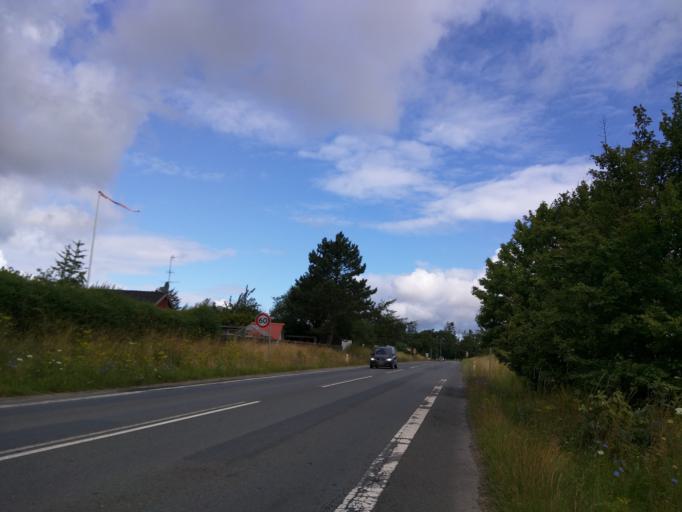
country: DK
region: Zealand
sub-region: Kalundborg Kommune
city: Svebolle
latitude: 55.6727
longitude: 11.2963
